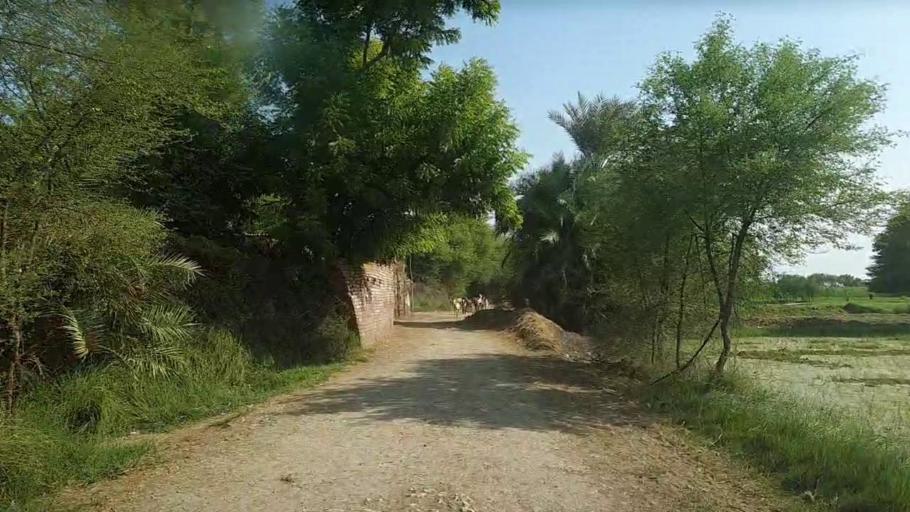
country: PK
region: Sindh
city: Mirpur Mathelo
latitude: 28.1168
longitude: 69.5892
